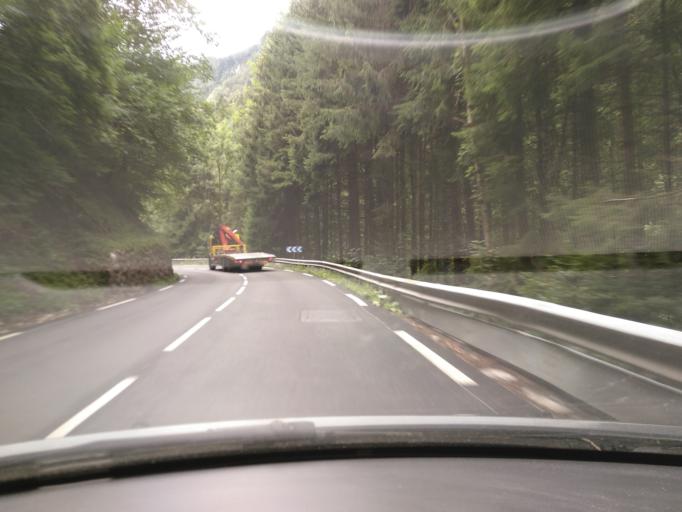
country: FR
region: Rhone-Alpes
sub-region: Departement de la Haute-Savoie
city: Saint-Jean-de-Sixt
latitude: 45.9735
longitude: 6.3847
